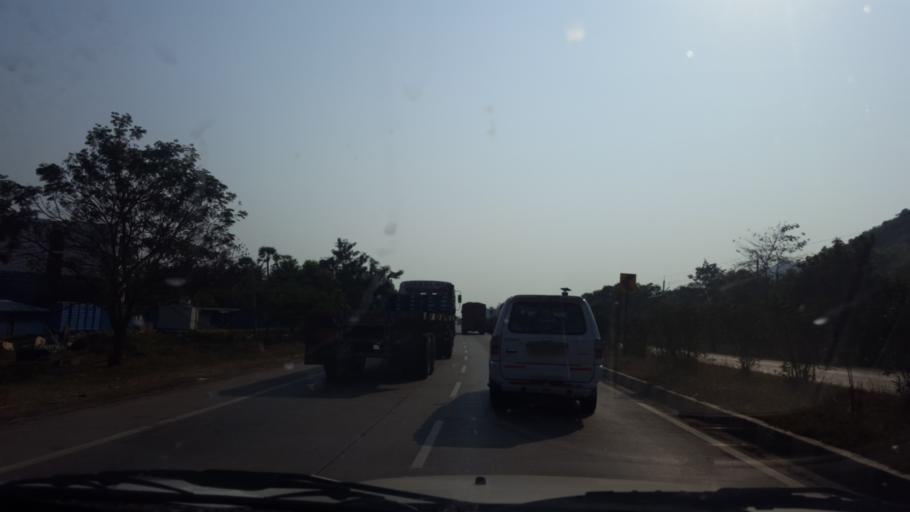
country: IN
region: Andhra Pradesh
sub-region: Vishakhapatnam
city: Elamanchili
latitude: 17.5550
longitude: 82.8449
